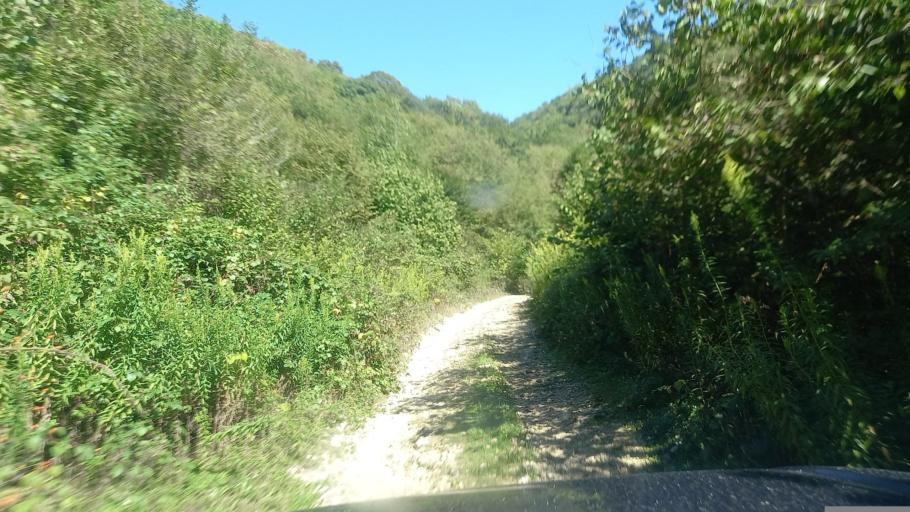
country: GE
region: Abkhazia
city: Dranda
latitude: 43.0327
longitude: 41.2820
